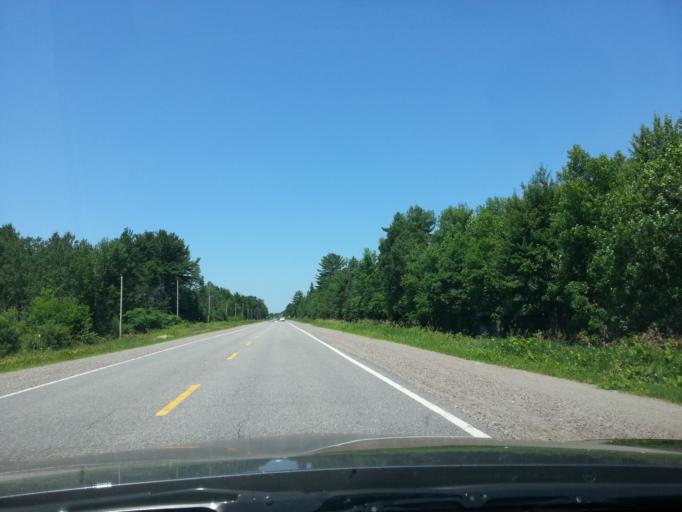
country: CA
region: Ontario
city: Arnprior
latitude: 45.5308
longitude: -76.3089
